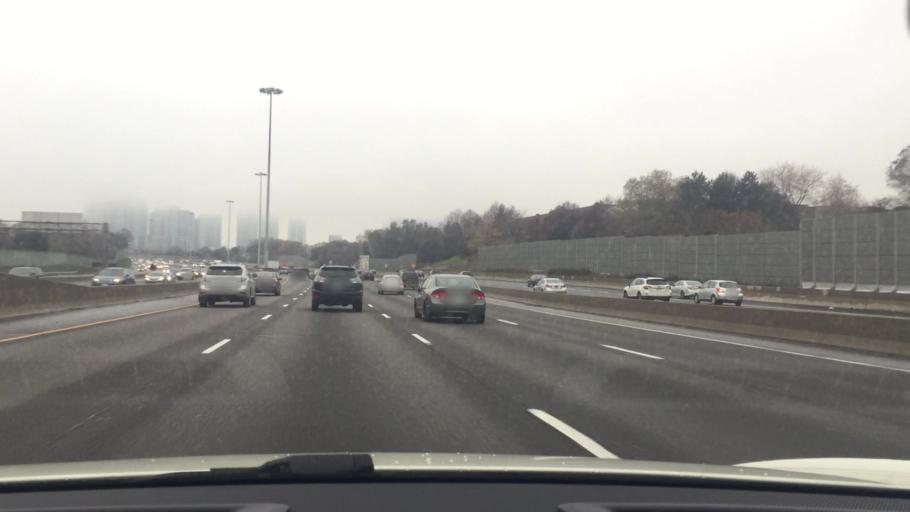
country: CA
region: Ontario
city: Willowdale
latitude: 43.7635
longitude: -79.3902
